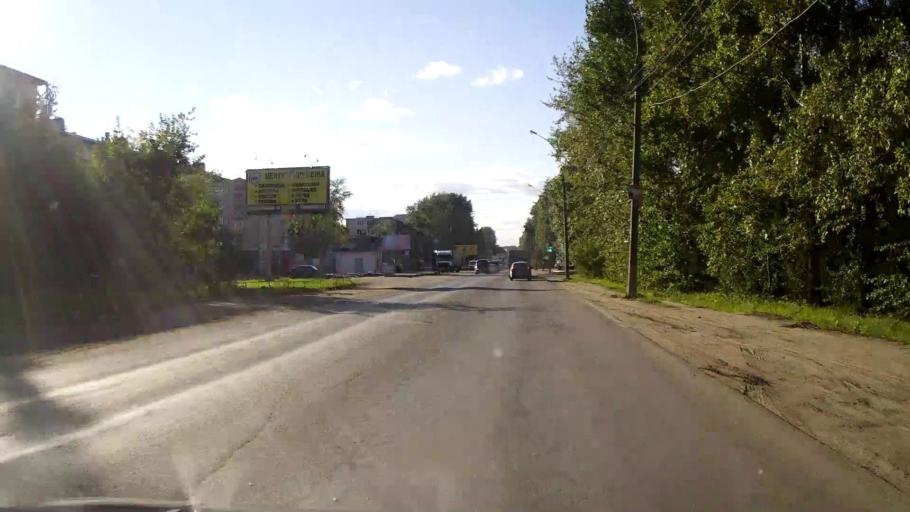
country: RU
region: Vologda
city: Vologda
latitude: 59.2053
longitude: 39.8646
